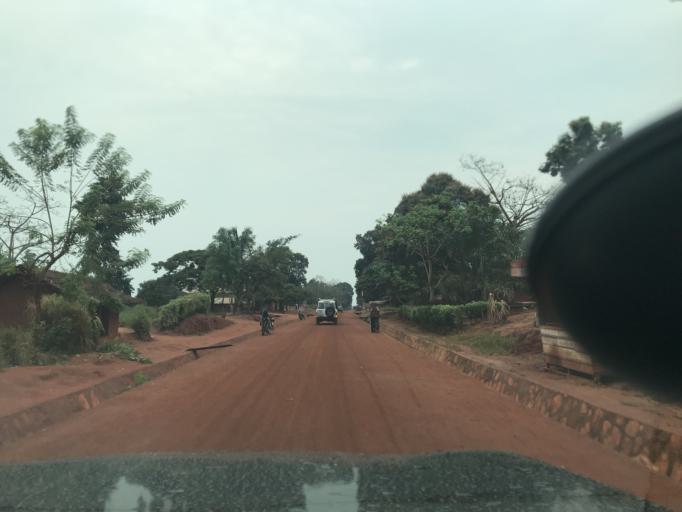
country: CD
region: Equateur
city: Gemena
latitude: 3.2215
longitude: 19.7783
